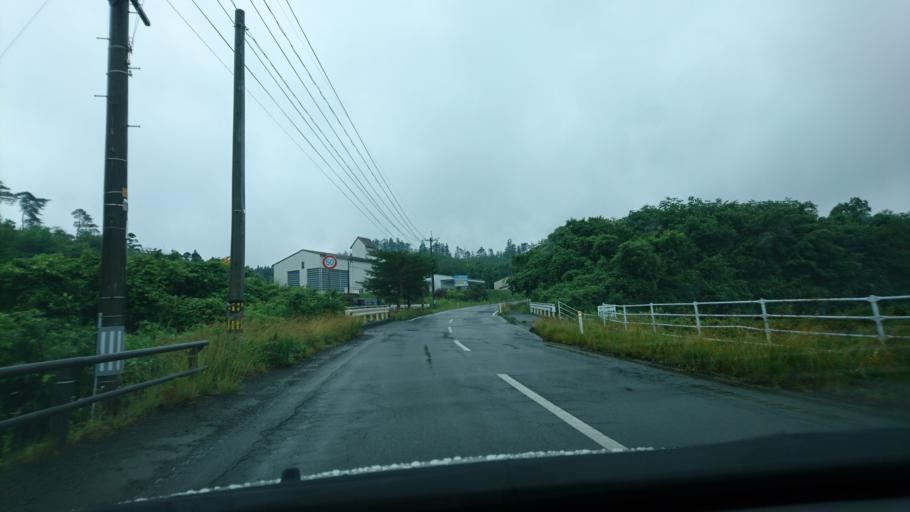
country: JP
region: Iwate
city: Ichinoseki
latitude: 38.9380
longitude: 141.0625
